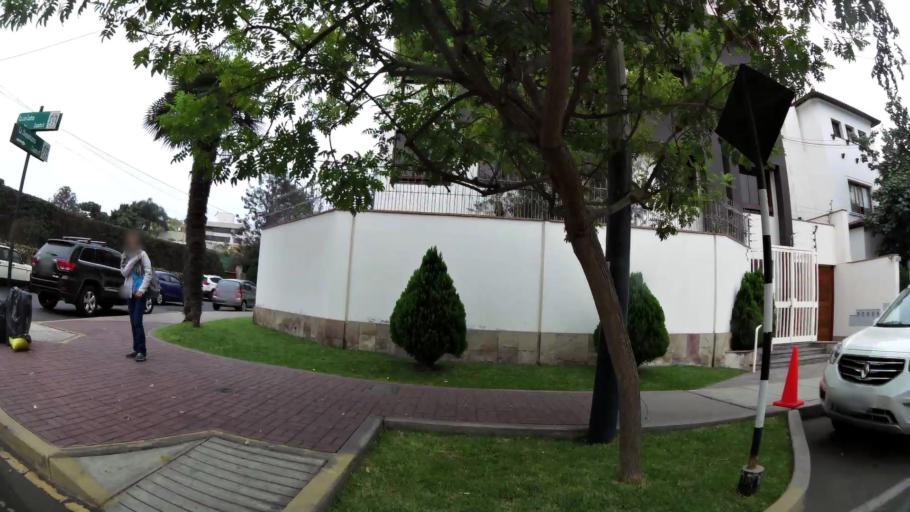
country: PE
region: Lima
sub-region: Lima
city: San Isidro
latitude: -12.0976
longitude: -77.0433
